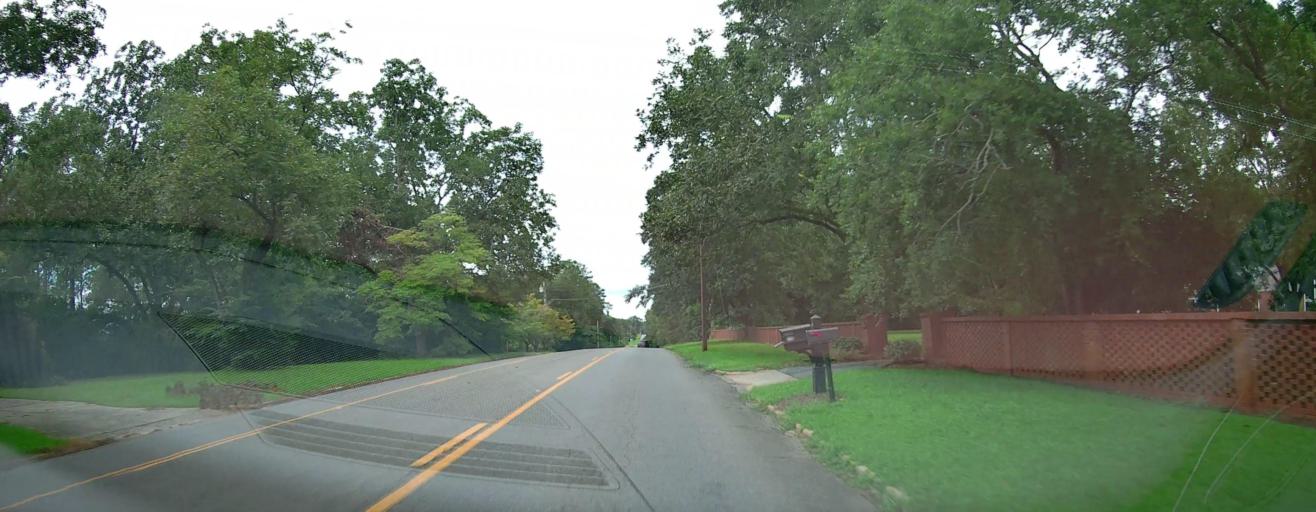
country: US
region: Georgia
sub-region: Schley County
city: Ellaville
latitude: 32.2401
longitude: -84.3159
